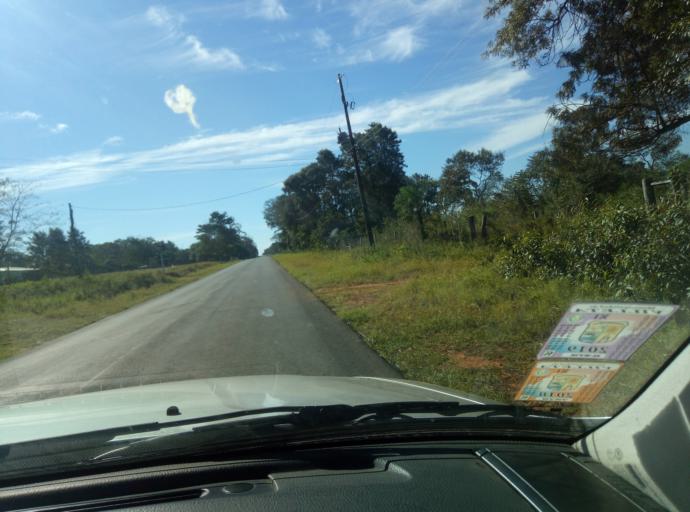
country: PY
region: Caaguazu
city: Carayao
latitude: -25.1681
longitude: -56.3130
